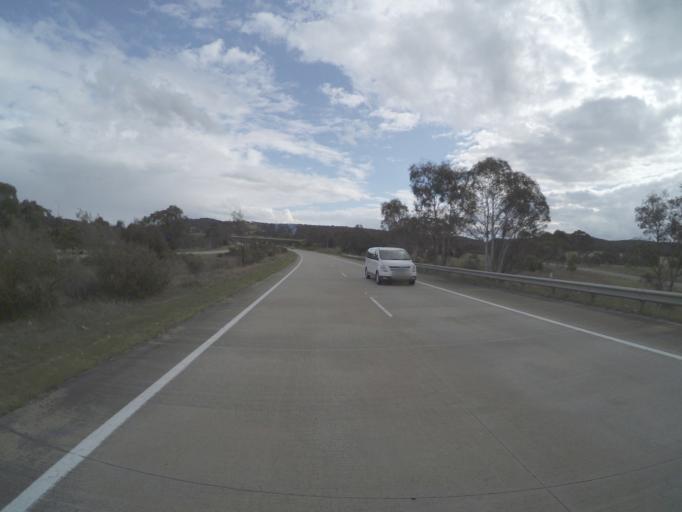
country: AU
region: New South Wales
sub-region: Goulburn Mulwaree
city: Goulburn
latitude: -34.7407
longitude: 149.7739
